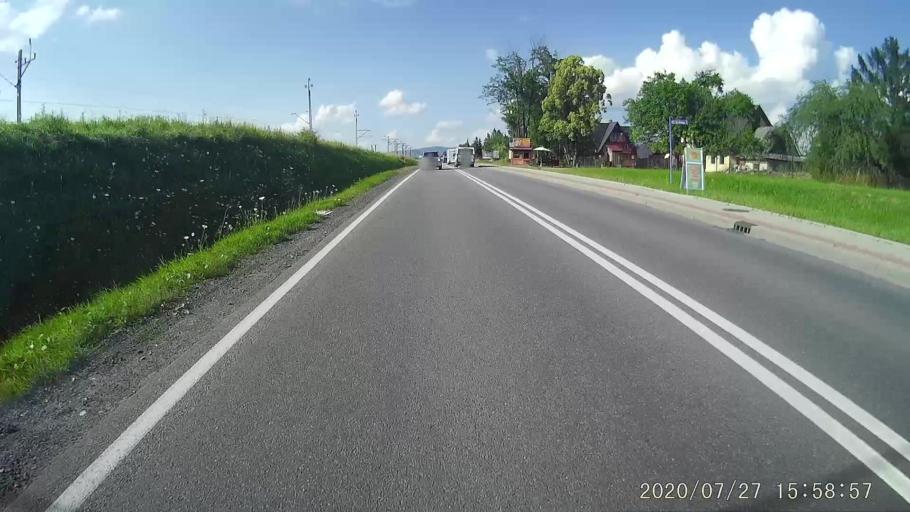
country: PL
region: Lesser Poland Voivodeship
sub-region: Powiat nowotarski
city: Szaflary
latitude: 49.4073
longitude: 20.0173
